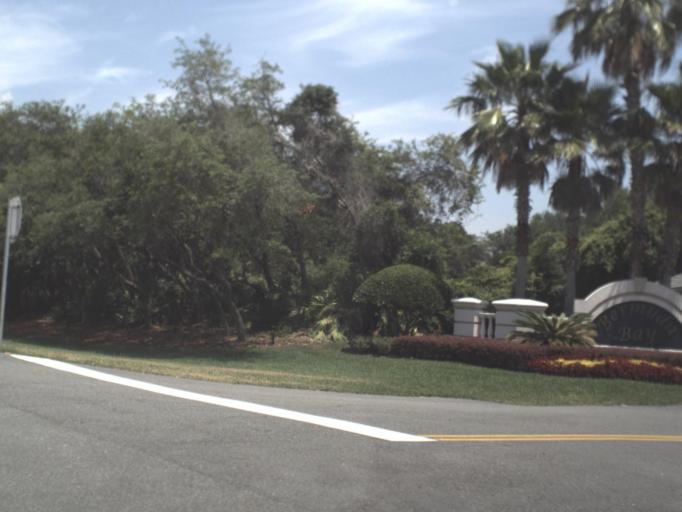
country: US
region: Florida
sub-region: Saint Johns County
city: Palm Valley
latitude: 30.1671
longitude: -81.3671
